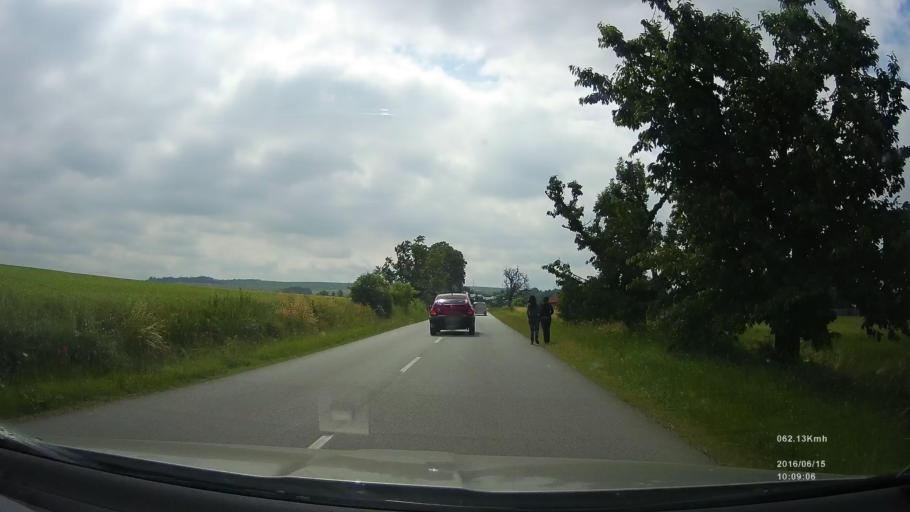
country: SK
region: Kosicky
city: Kosice
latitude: 48.7611
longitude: 21.3372
